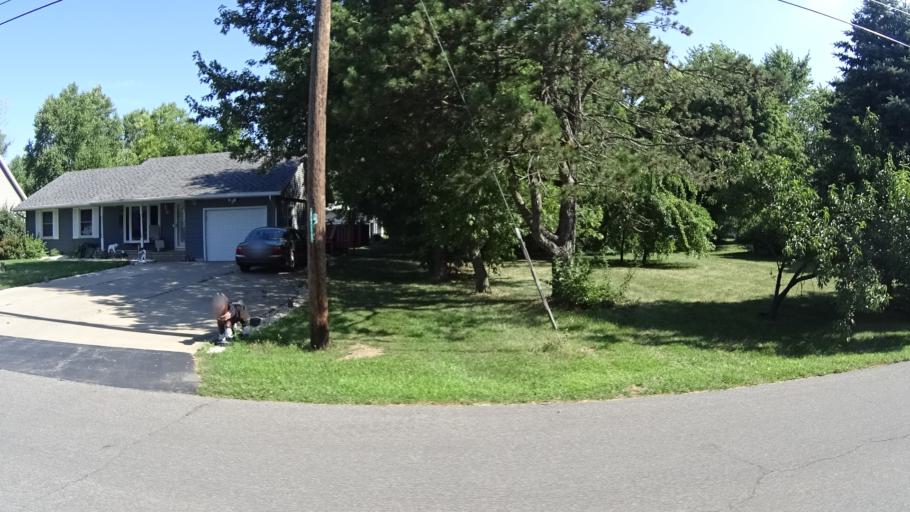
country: US
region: Ohio
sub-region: Huron County
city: Bellevue
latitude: 41.3719
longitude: -82.7962
